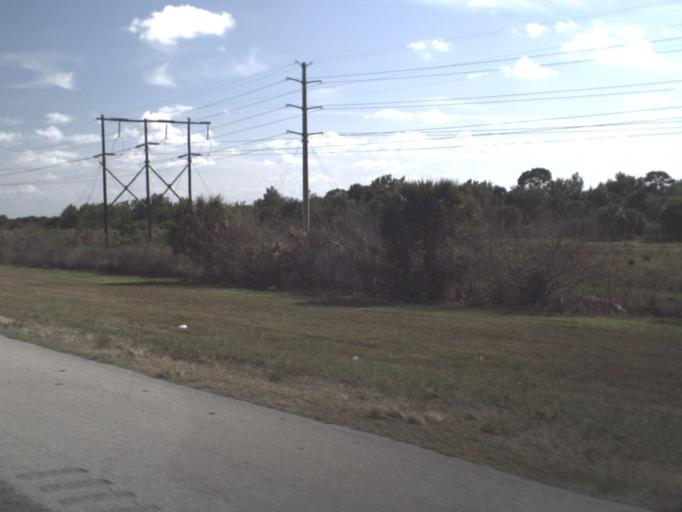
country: US
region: Florida
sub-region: Brevard County
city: June Park
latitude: 28.1078
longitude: -80.7061
